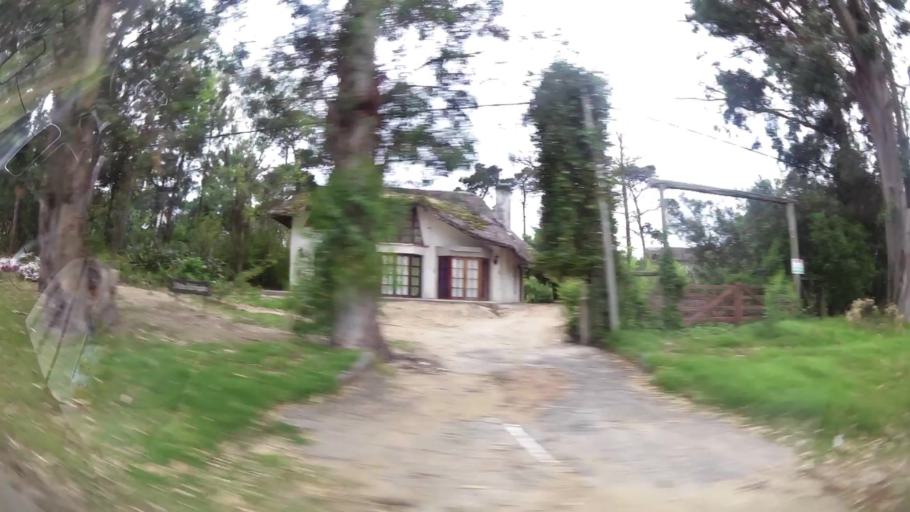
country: UY
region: Maldonado
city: Maldonado
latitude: -34.9020
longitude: -54.9981
